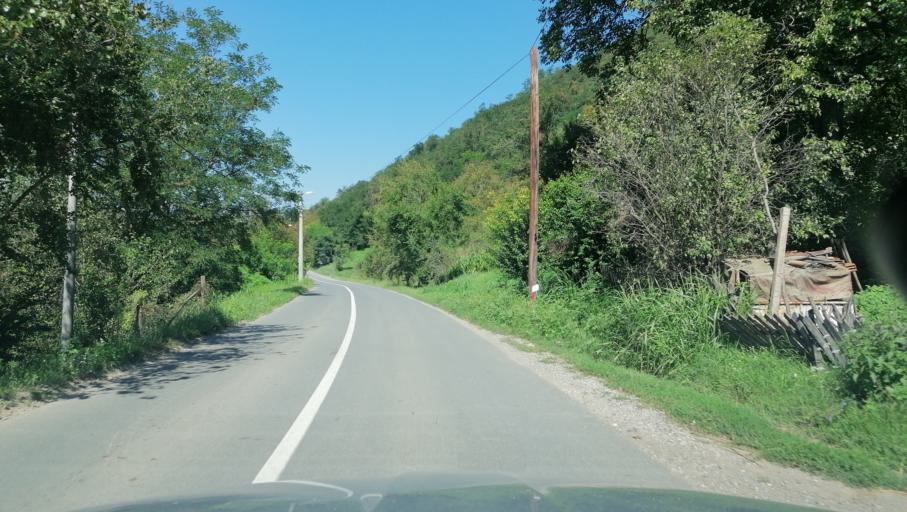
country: RS
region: Central Serbia
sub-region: Raski Okrug
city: Vrnjacka Banja
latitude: 43.6595
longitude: 20.9310
